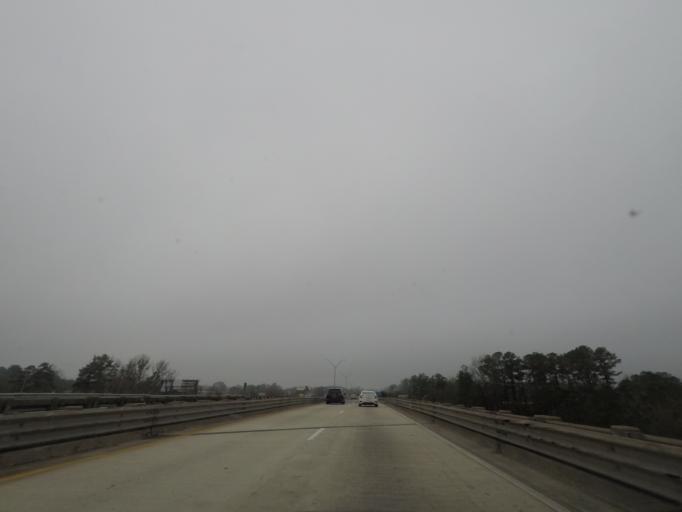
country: US
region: North Carolina
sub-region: Robeson County
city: Lumberton
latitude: 34.6278
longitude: -79.0398
